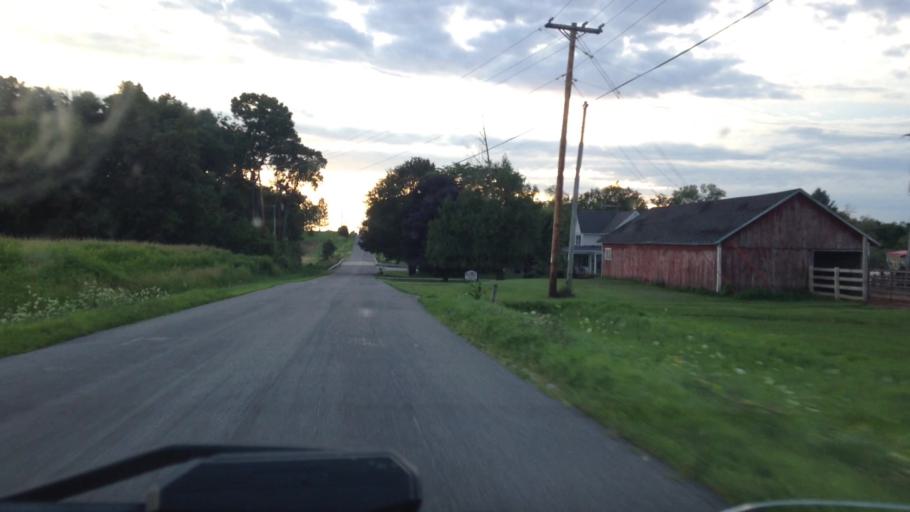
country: US
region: Wisconsin
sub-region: Dodge County
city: Mayville
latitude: 43.4932
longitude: -88.5083
